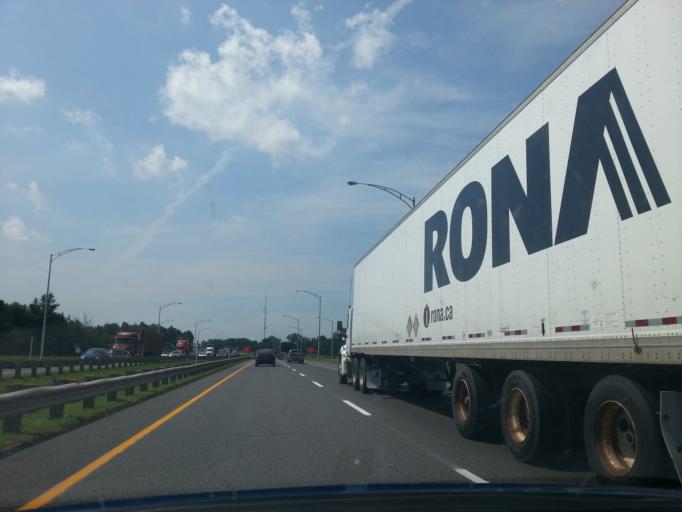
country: CA
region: Quebec
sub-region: Centre-du-Quebec
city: Drummondville
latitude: 45.9106
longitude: -72.5026
